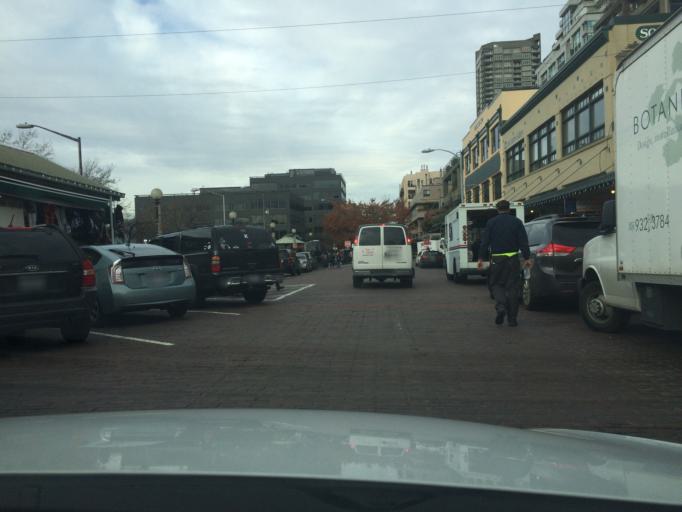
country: US
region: Washington
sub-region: King County
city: Seattle
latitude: 47.6099
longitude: -122.3426
